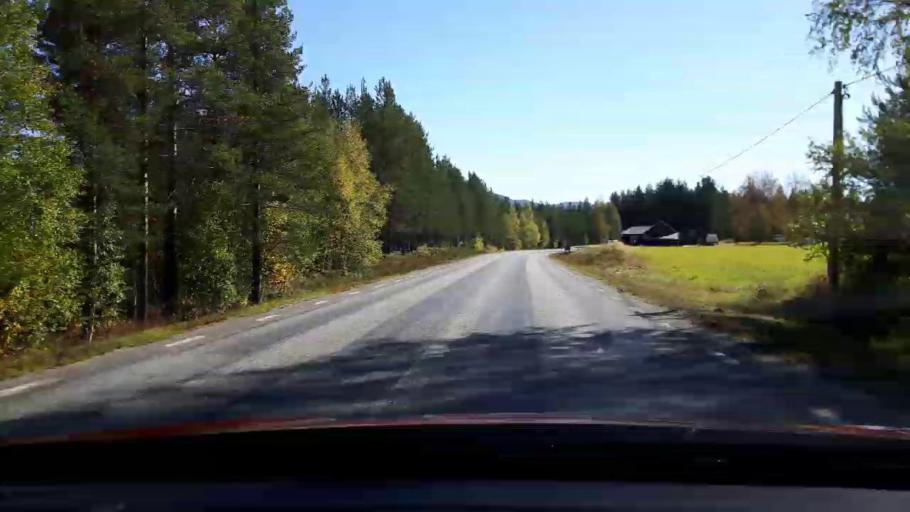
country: SE
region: Jaemtland
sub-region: Harjedalens Kommun
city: Sveg
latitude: 62.3632
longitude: 13.9995
